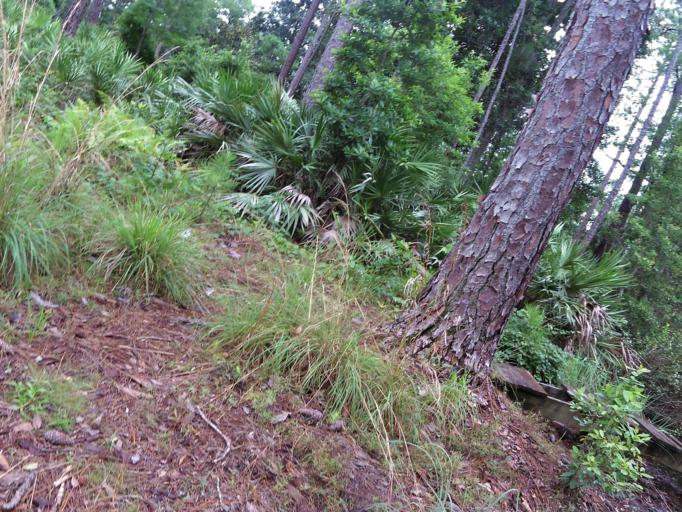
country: US
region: Florida
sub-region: Clay County
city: Green Cove Springs
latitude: 29.9761
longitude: -81.6385
